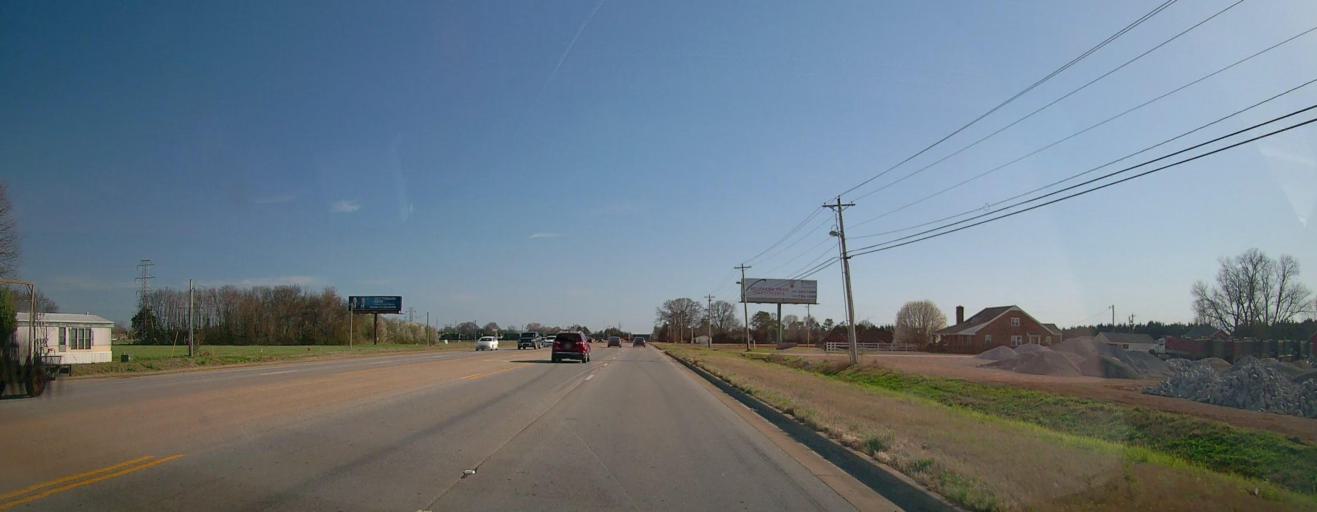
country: US
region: Alabama
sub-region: Colbert County
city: Muscle Shoals
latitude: 34.7204
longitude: -87.6350
